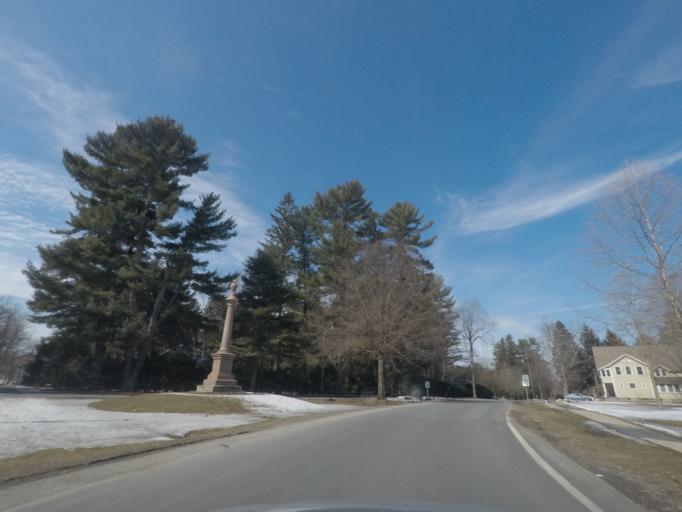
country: US
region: Massachusetts
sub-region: Berkshire County
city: Stockbridge
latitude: 42.2841
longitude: -73.3200
